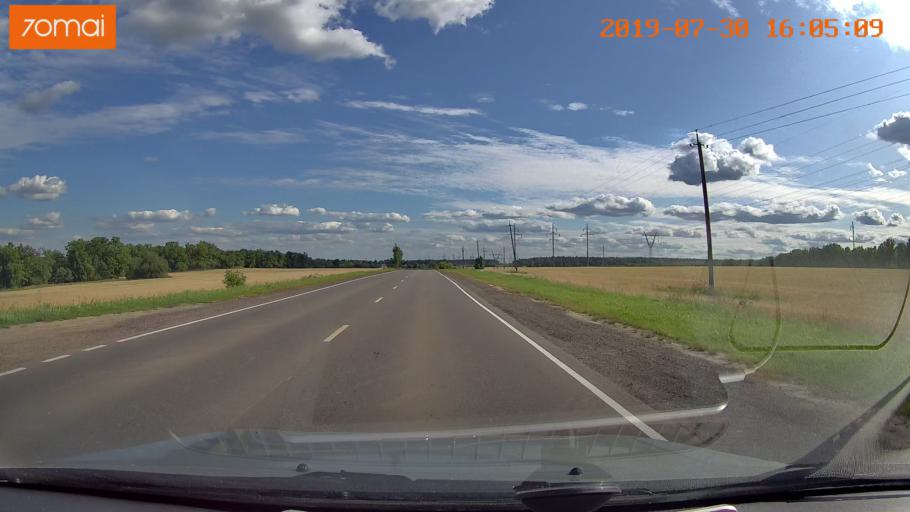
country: RU
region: Moskovskaya
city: Lopatinskiy
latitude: 55.2702
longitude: 38.7140
